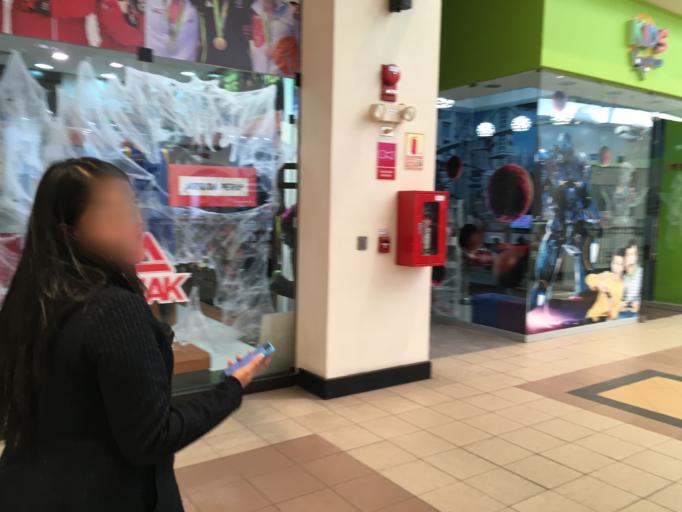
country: PE
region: Arequipa
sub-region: Provincia de Arequipa
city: Arequipa
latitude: -16.4108
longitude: -71.5209
